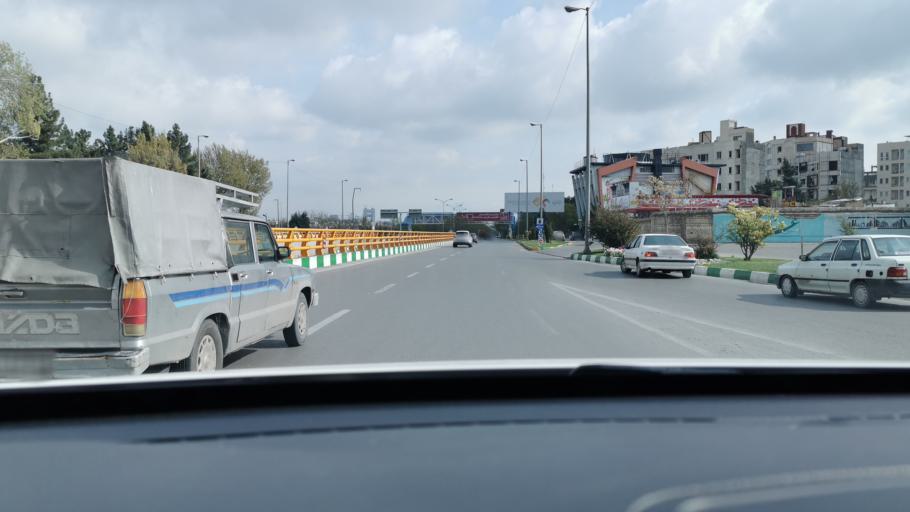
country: IR
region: Razavi Khorasan
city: Mashhad
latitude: 36.2871
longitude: 59.5573
